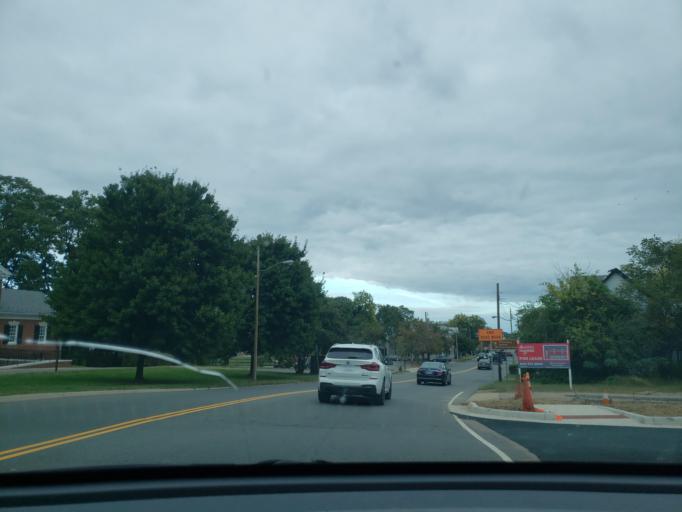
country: US
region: Virginia
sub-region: City of Fredericksburg
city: Fredericksburg
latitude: 38.2933
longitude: -77.4675
